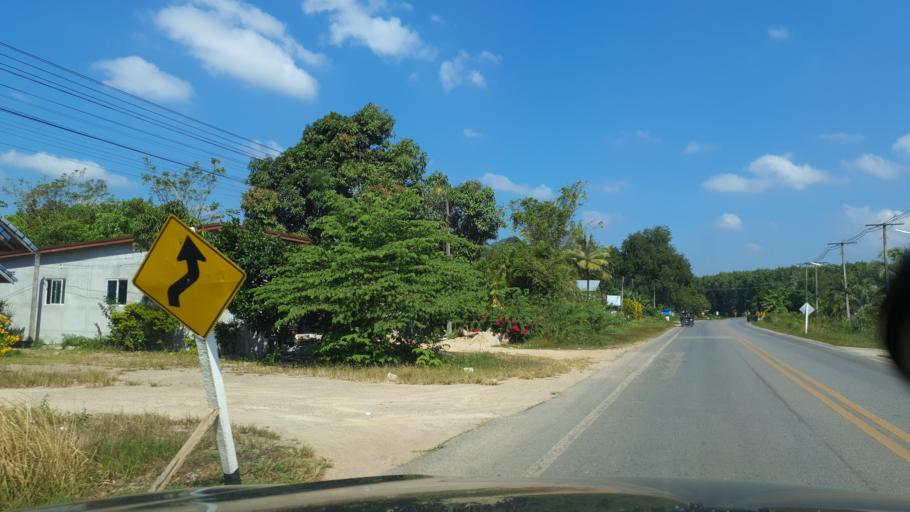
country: TH
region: Phangnga
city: Ban Ao Nang
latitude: 8.0616
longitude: 98.8593
